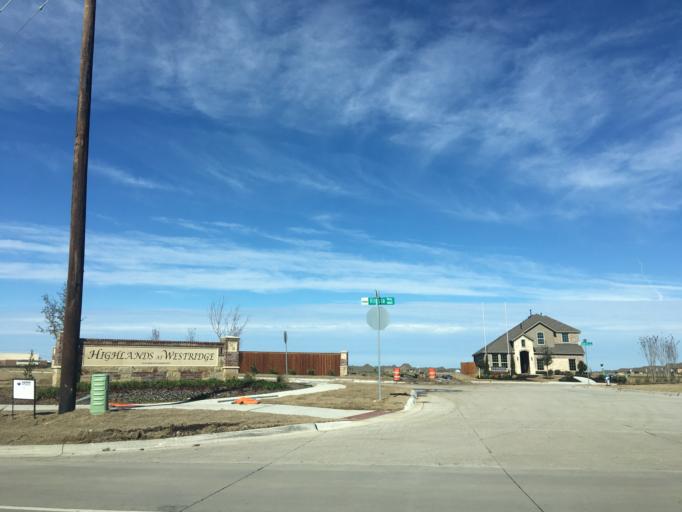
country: US
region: Texas
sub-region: Collin County
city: Prosper
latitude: 33.2037
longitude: -96.7653
